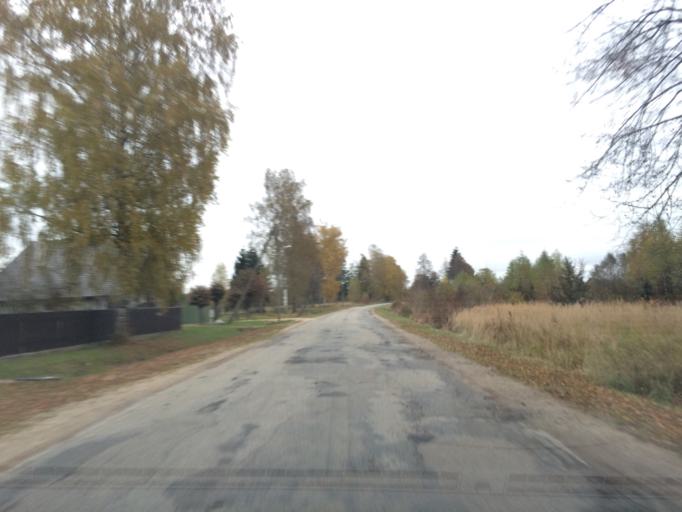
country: LV
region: Plavinu
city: Plavinas
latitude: 56.6164
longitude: 25.7629
